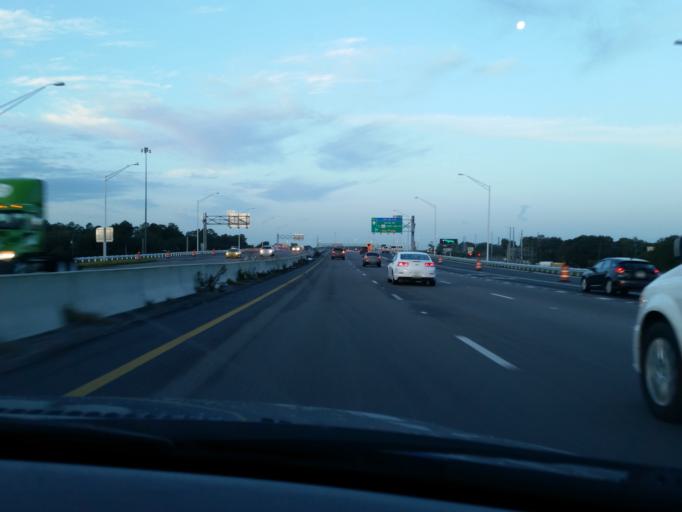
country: US
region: Florida
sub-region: Orange County
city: Belle Isle
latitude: 28.4510
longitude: -81.3360
